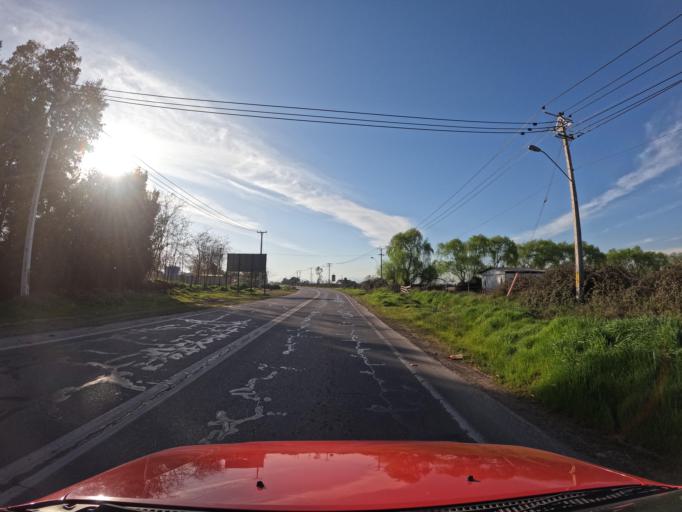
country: CL
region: Maule
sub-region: Provincia de Curico
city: Teno
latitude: -34.8730
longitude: -71.0848
